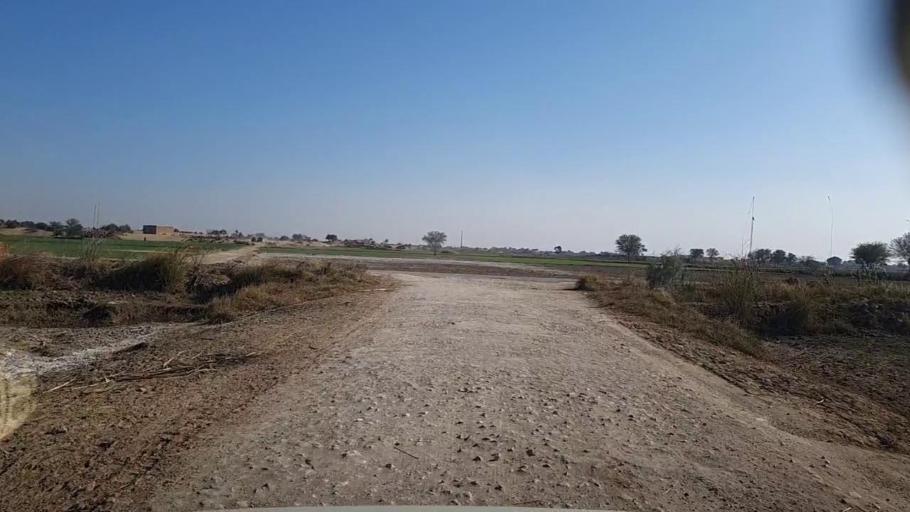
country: PK
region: Sindh
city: Khairpur
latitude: 27.9249
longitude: 69.7367
